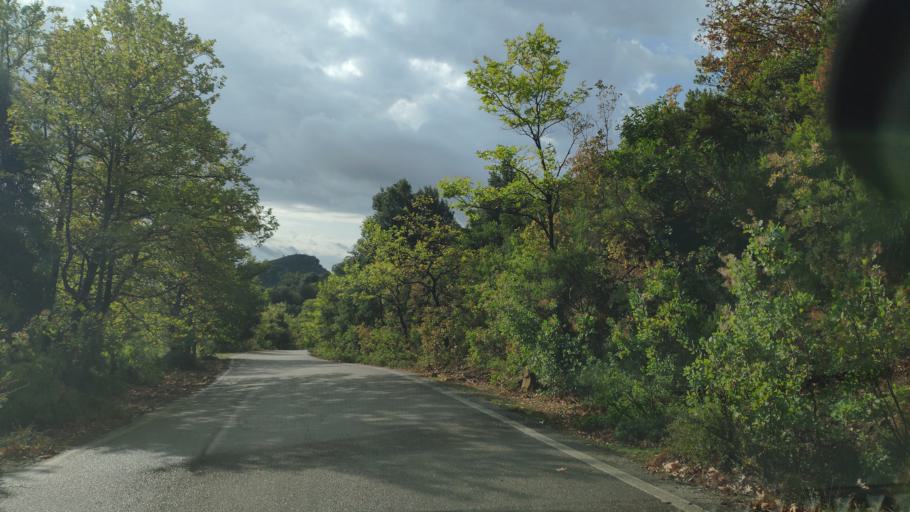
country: GR
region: West Greece
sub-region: Nomos Aitolias kai Akarnanias
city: Sardinia
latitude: 38.8612
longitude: 21.3036
